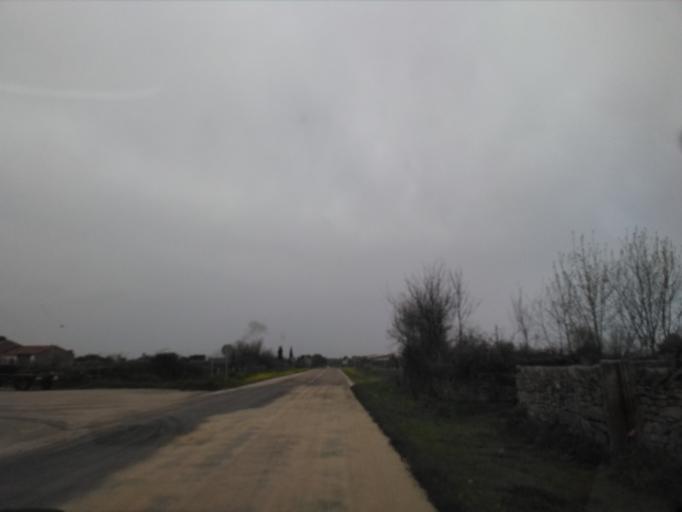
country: ES
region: Castille and Leon
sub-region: Provincia de Salamanca
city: Yecla de Yeltes
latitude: 40.9579
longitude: -6.4909
